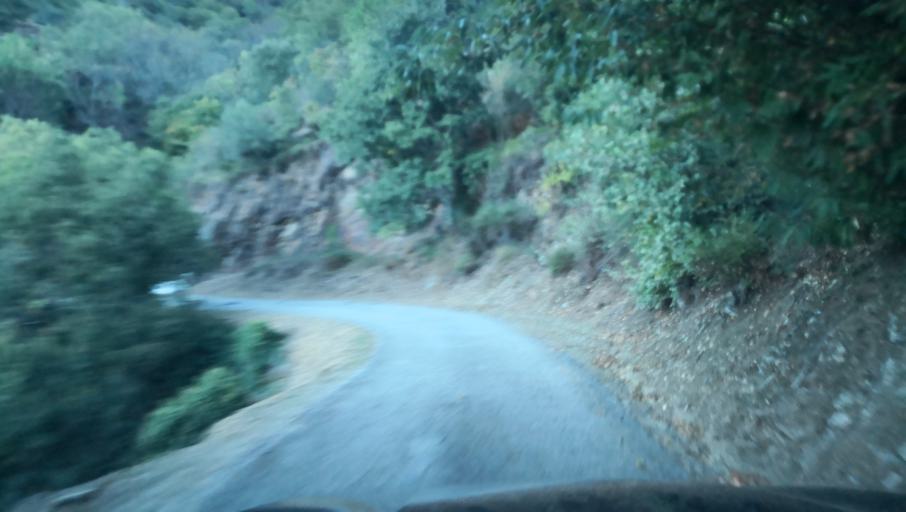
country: PT
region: Vila Real
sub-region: Santa Marta de Penaguiao
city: Santa Marta de Penaguiao
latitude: 41.2588
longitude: -7.8226
